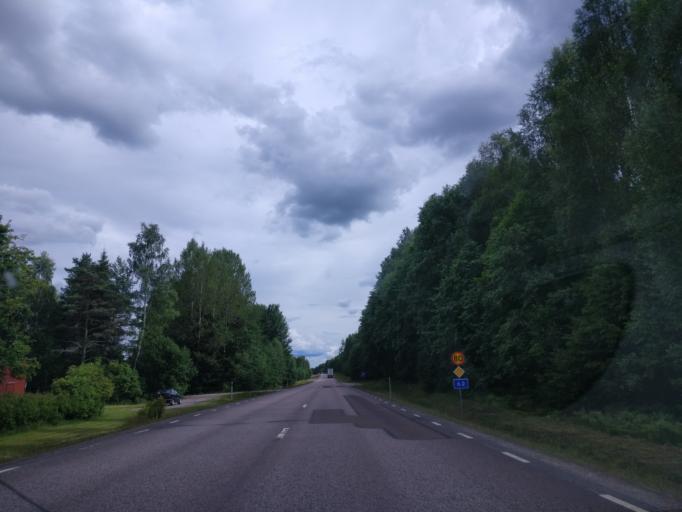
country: SE
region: Vaermland
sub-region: Hagfors Kommun
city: Ekshaerad
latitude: 60.1544
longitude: 13.5170
